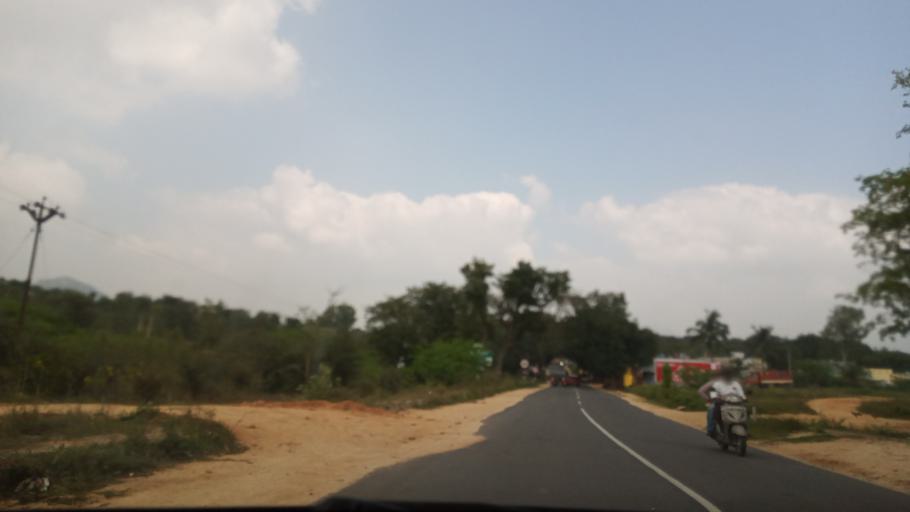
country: IN
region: Andhra Pradesh
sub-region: Chittoor
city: Madanapalle
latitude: 13.5910
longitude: 78.5258
